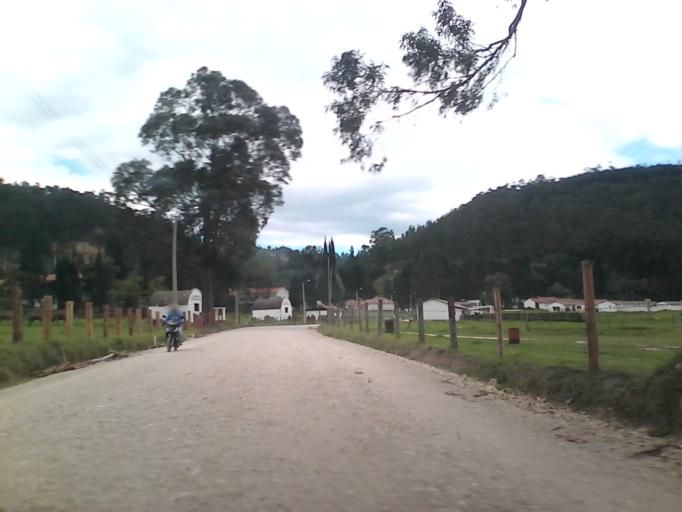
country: CO
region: Boyaca
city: Duitama
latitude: 5.8087
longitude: -73.0672
